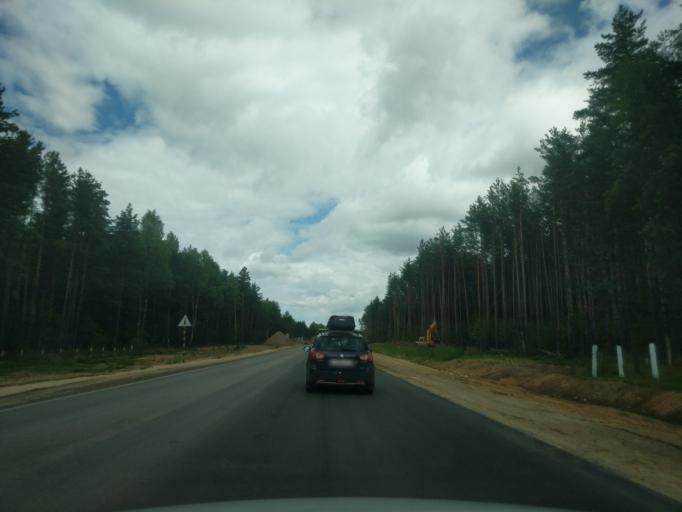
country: RU
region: Jaroslavl
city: Levashevo
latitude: 57.6803
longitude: 40.5950
